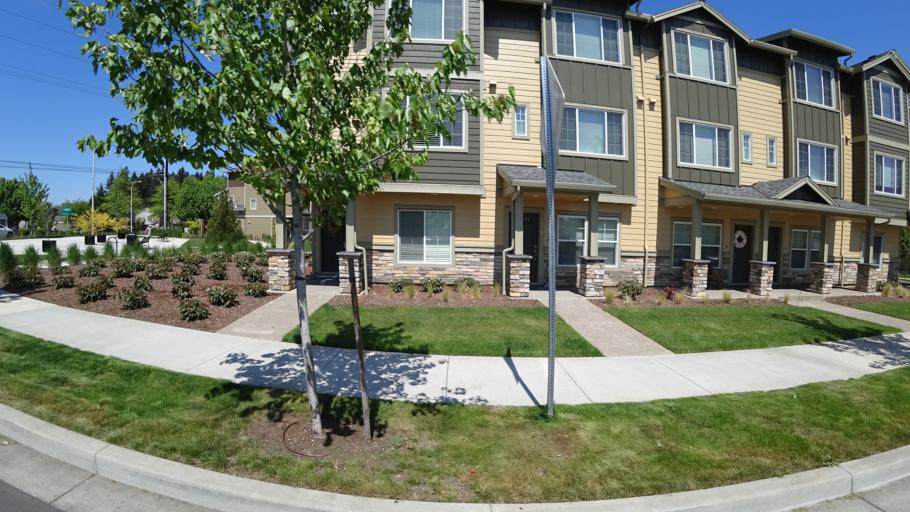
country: US
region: Oregon
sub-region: Washington County
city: Aloha
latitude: 45.5167
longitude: -122.8992
